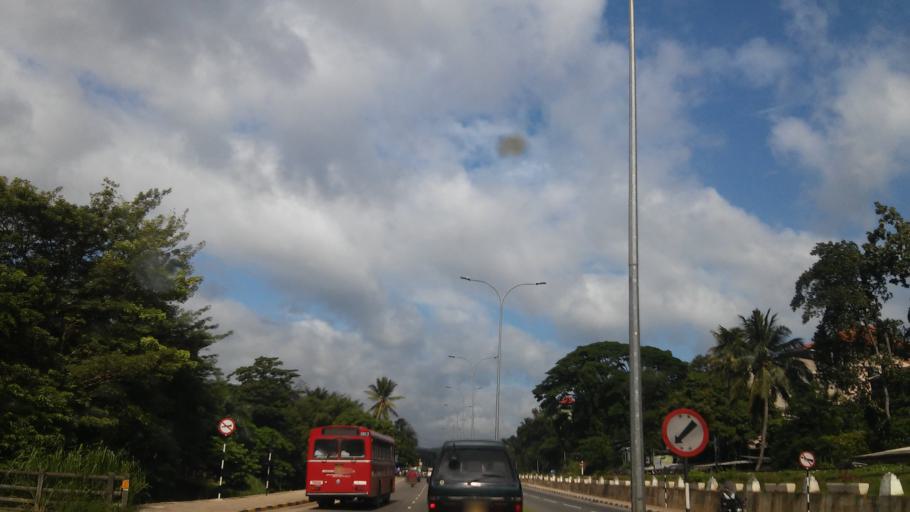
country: LK
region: Central
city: Kandy
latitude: 7.2738
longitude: 80.6117
